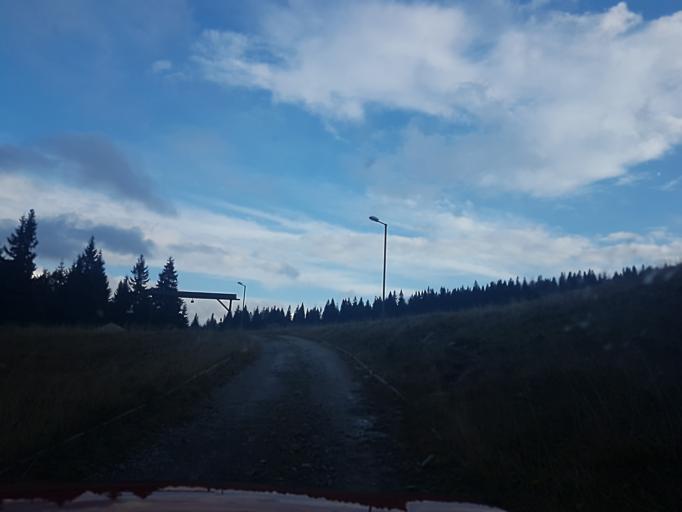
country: SK
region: Zilinsky
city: Ruzomberok
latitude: 48.9903
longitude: 19.2005
